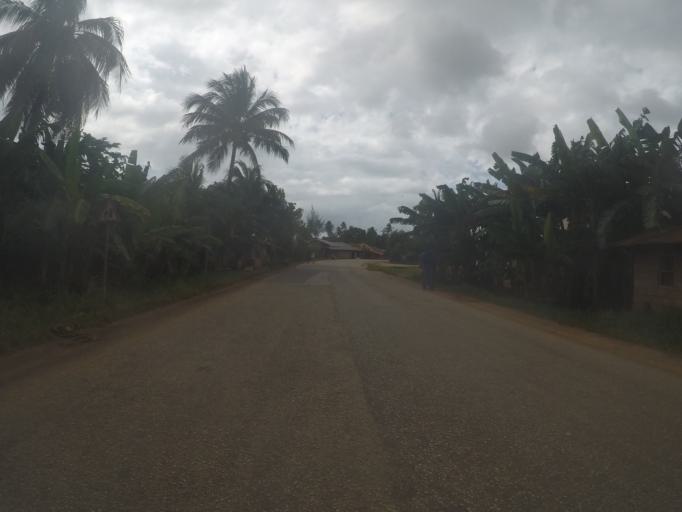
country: TZ
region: Zanzibar North
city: Gamba
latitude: -5.9311
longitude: 39.2545
